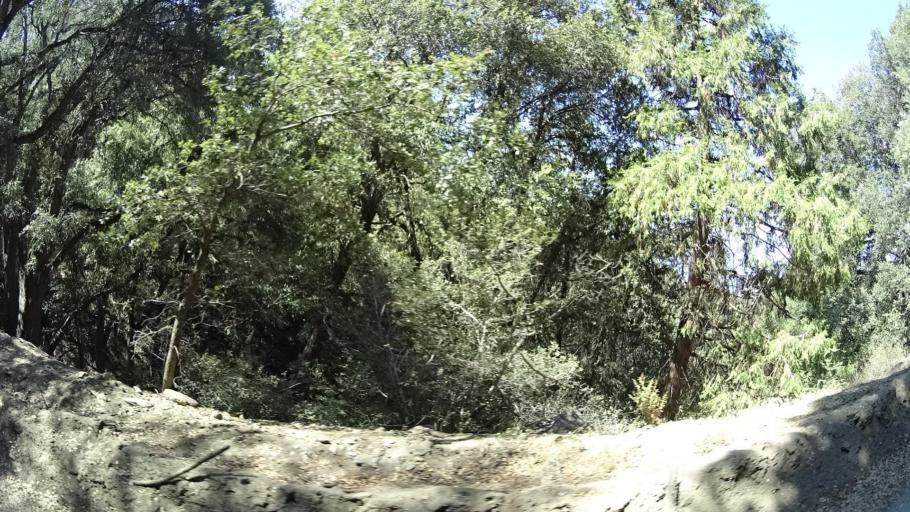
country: US
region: California
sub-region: Riverside County
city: Aguanga
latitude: 33.3402
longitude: -116.9240
